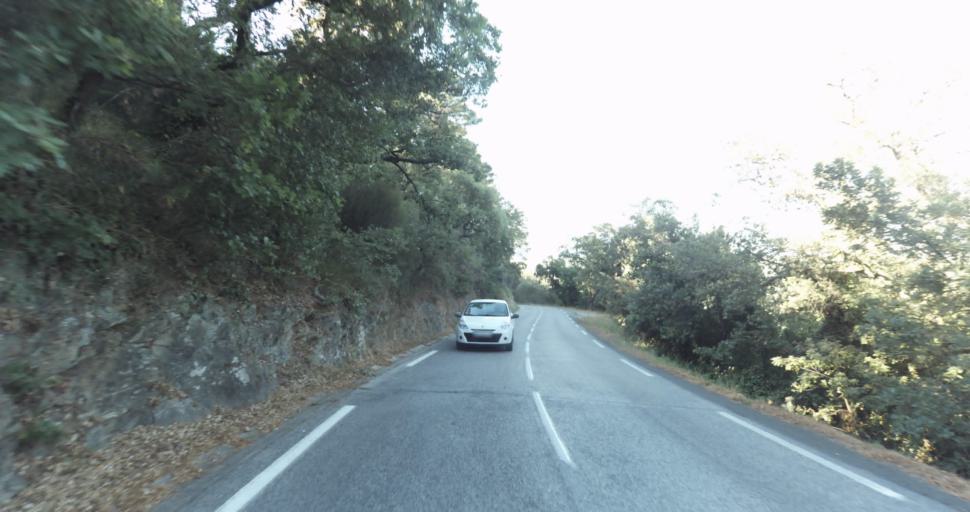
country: FR
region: Provence-Alpes-Cote d'Azur
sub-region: Departement du Var
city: Gassin
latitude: 43.2362
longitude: 6.5861
